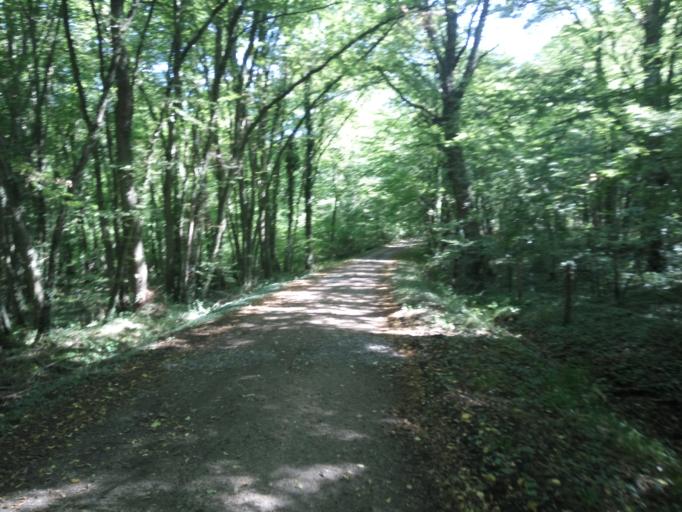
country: FR
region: Auvergne
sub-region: Departement de l'Allier
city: Brugheas
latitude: 46.0882
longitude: 3.3561
